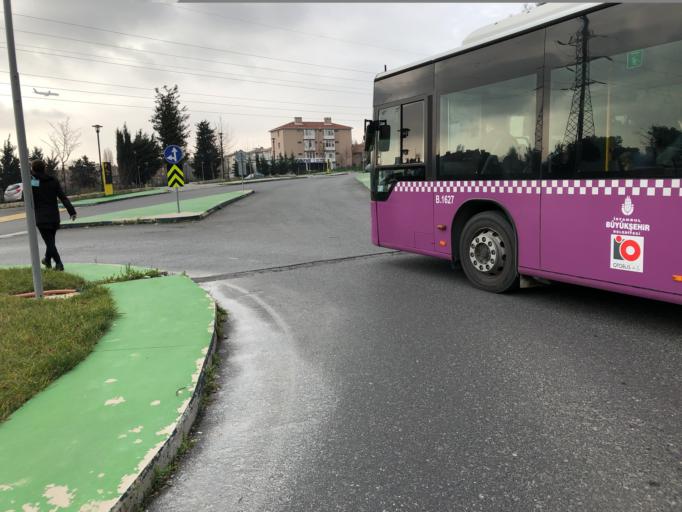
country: TR
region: Istanbul
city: merter keresteciler
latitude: 41.0196
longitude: 28.8920
